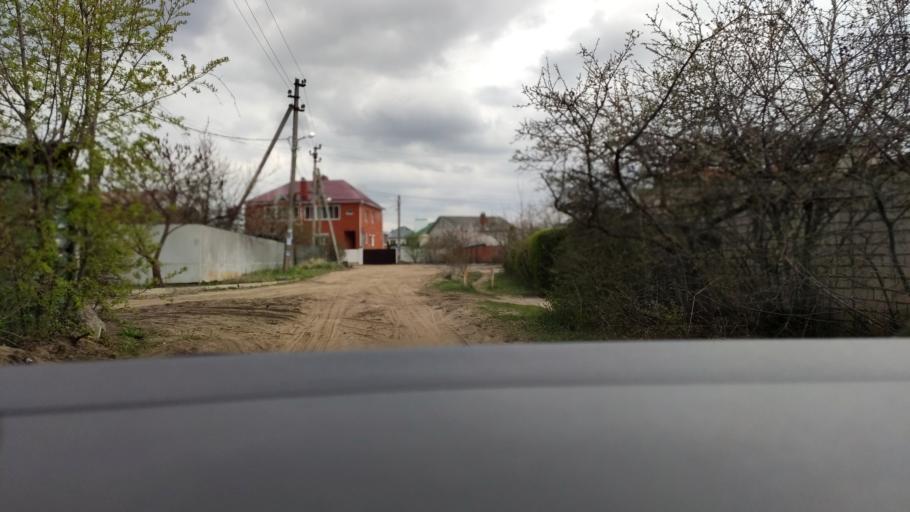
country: RU
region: Voronezj
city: Pridonskoy
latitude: 51.6564
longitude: 39.0916
